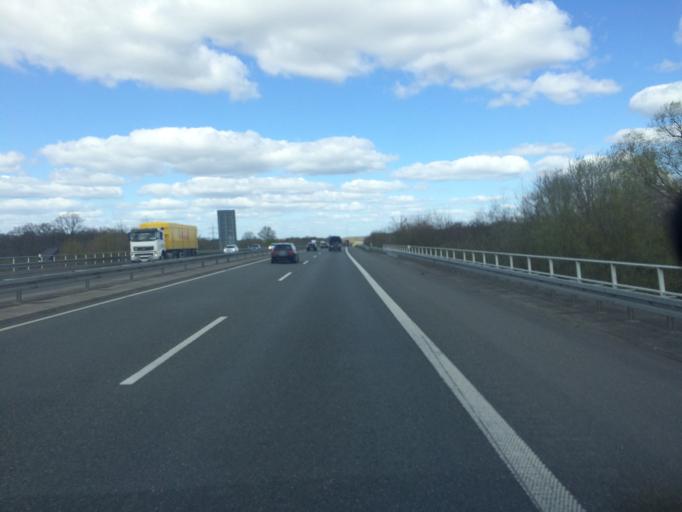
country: DE
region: North Rhine-Westphalia
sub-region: Regierungsbezirk Munster
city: Ochtrup
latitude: 52.2048
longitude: 7.1231
